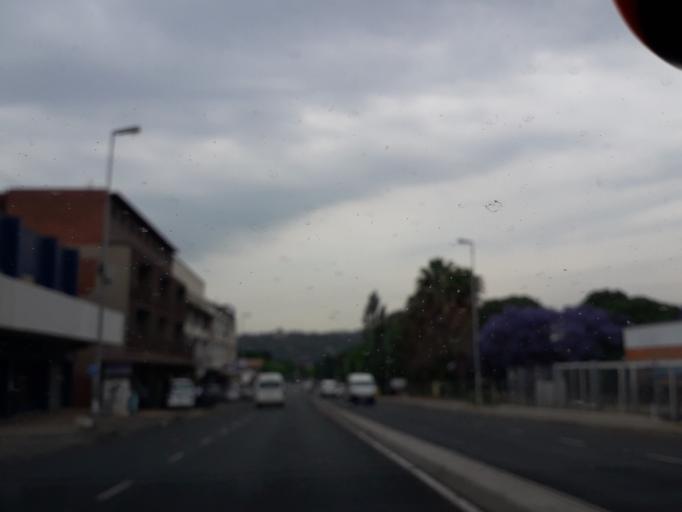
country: ZA
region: Gauteng
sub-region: City of Johannesburg Metropolitan Municipality
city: Johannesburg
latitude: -26.1469
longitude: 28.0867
